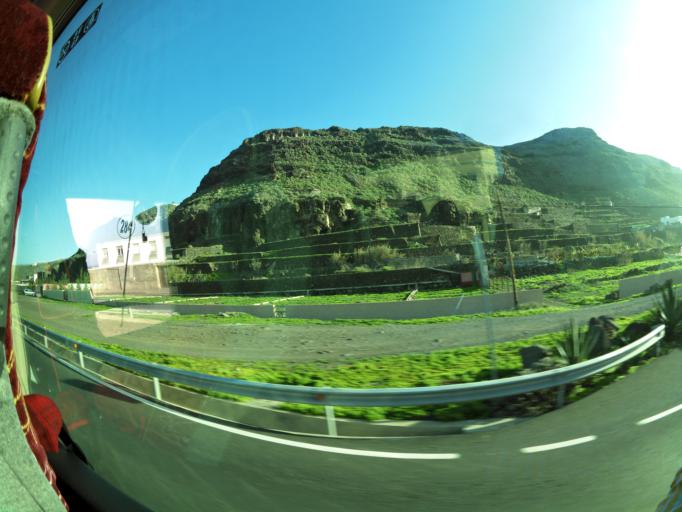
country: ES
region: Canary Islands
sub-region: Provincia de Las Palmas
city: Arucas
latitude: 28.1453
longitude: -15.5531
